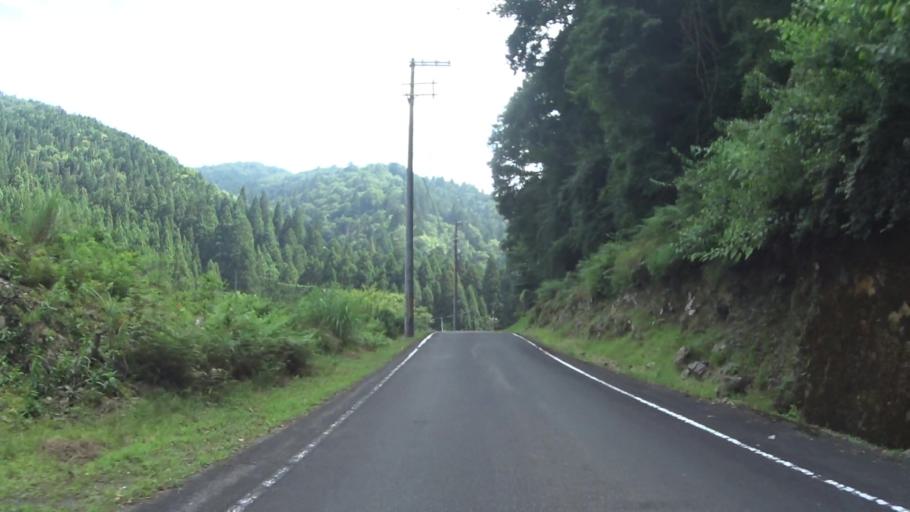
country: JP
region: Fukui
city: Obama
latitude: 35.3451
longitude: 135.6505
